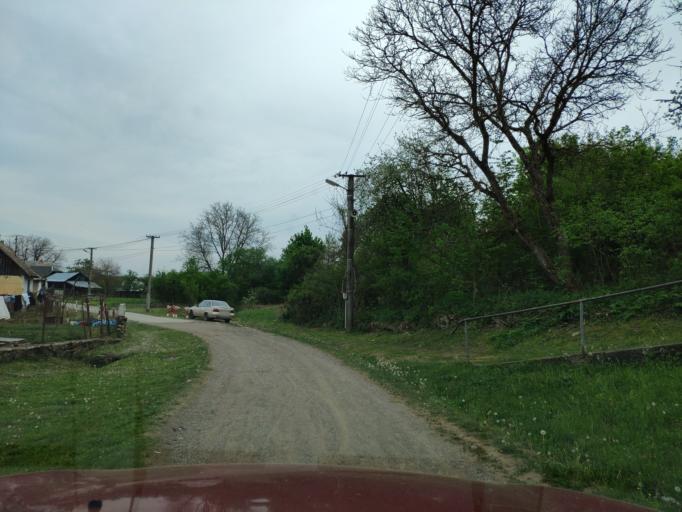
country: SK
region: Banskobystricky
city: Revuca
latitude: 48.5144
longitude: 20.1721
